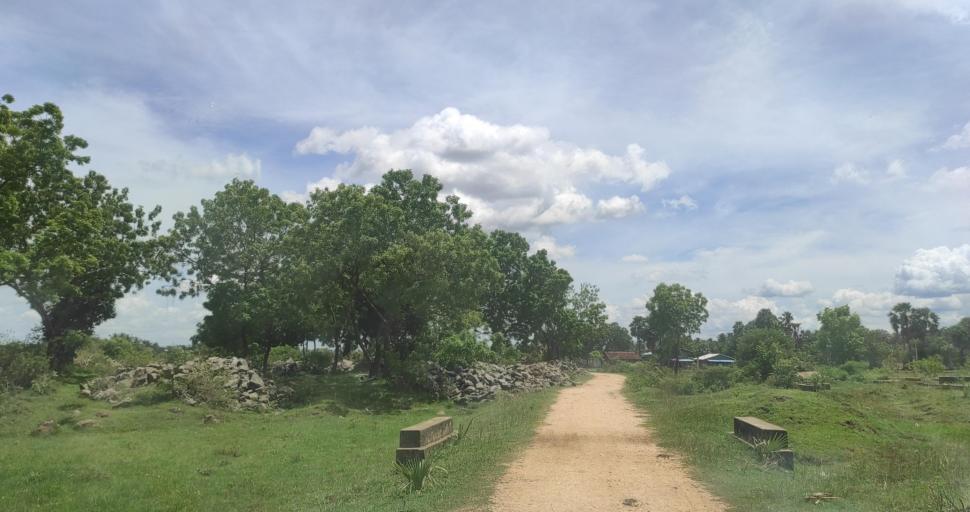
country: LK
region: Eastern Province
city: Trincomalee
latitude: 8.4441
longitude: 81.0485
